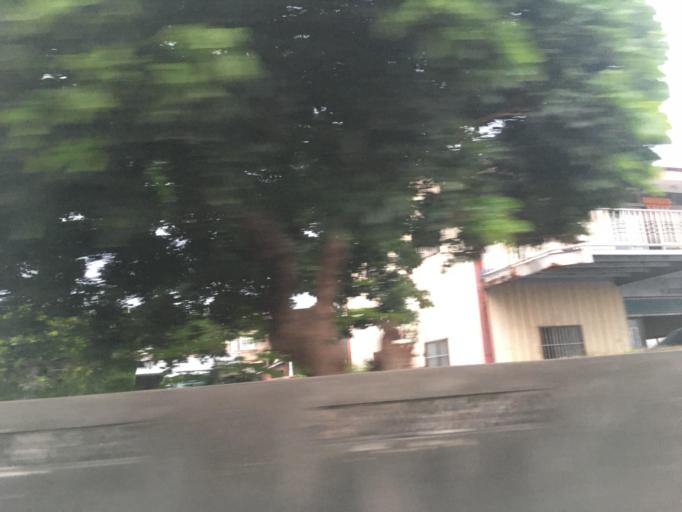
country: TW
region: Taiwan
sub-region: Yunlin
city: Douliu
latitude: 23.7024
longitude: 120.4428
